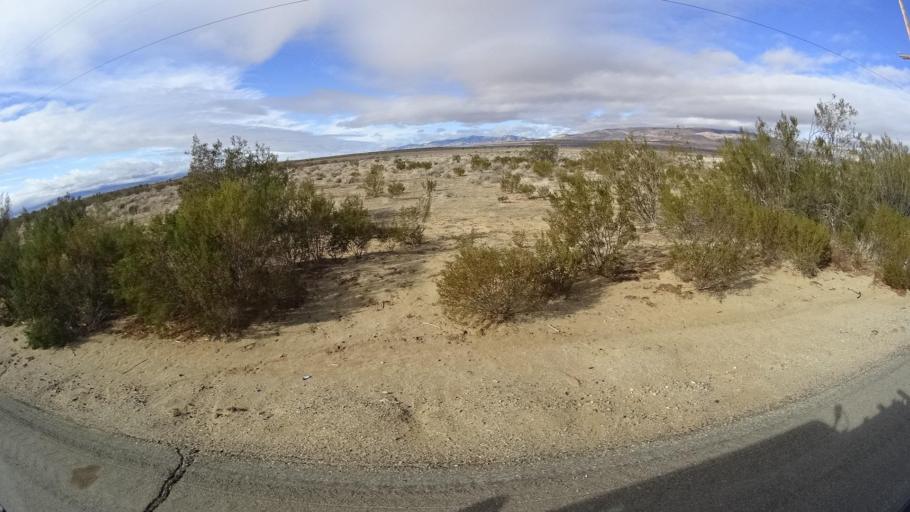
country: US
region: California
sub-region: Kern County
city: Rosamond
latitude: 34.9337
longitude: -118.2916
